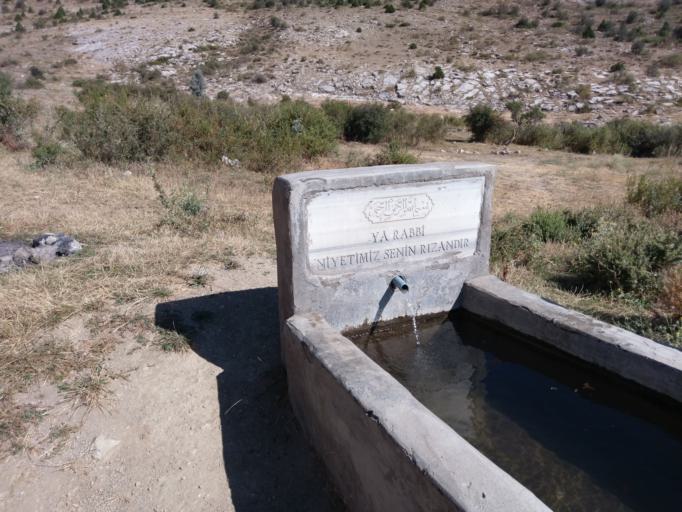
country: TR
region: Kayseri
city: Toklar
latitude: 38.4134
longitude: 36.1389
